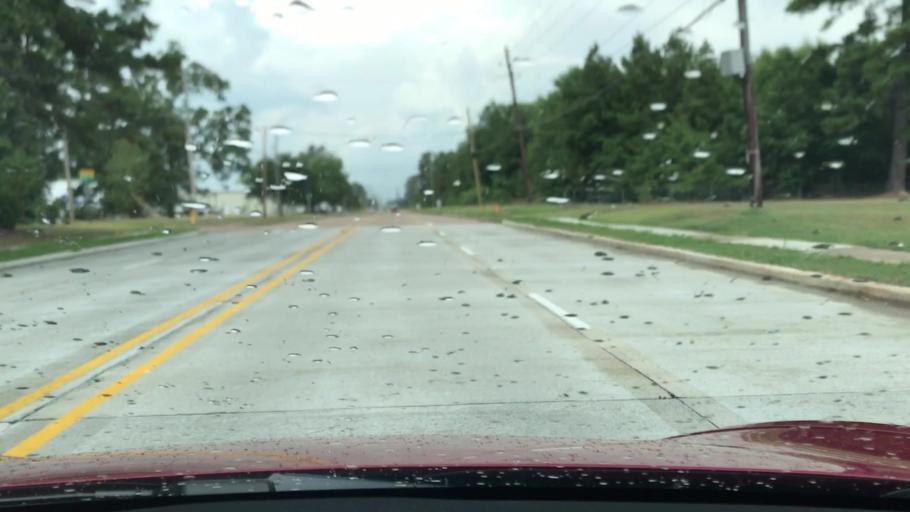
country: US
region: Louisiana
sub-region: Bossier Parish
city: Bossier City
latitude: 32.4083
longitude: -93.7632
